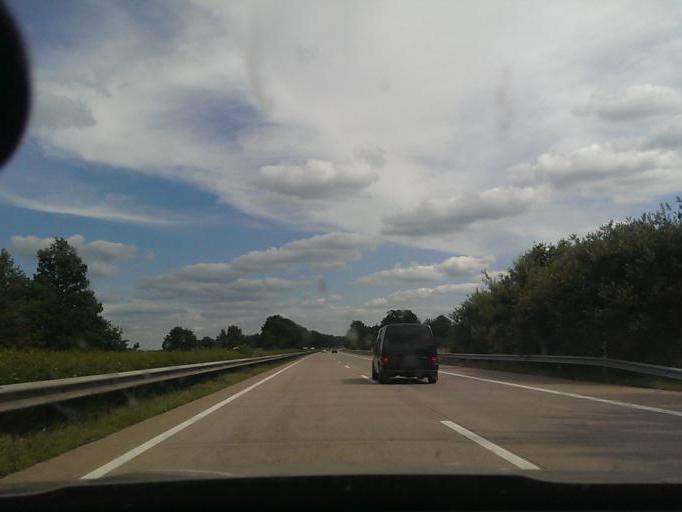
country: DE
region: Lower Saxony
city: Walsrode
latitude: 52.8658
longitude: 9.5289
